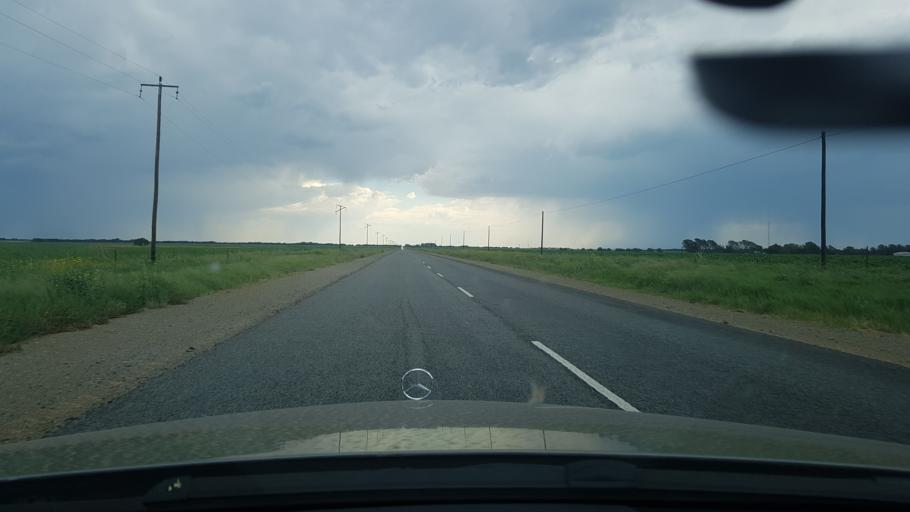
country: ZA
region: Orange Free State
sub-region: Lejweleputswa District Municipality
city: Hoopstad
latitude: -27.9684
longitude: 25.6833
